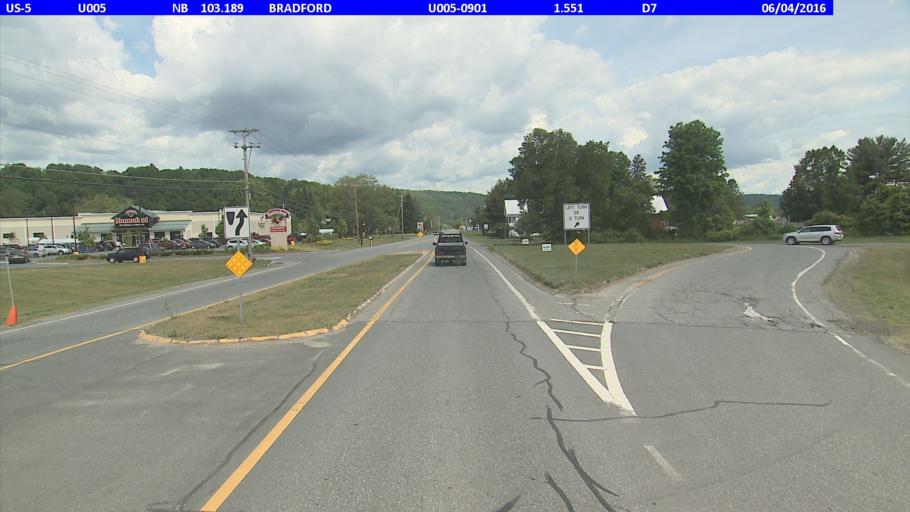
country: US
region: New Hampshire
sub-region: Grafton County
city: Haverhill
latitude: 43.9832
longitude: -72.1213
